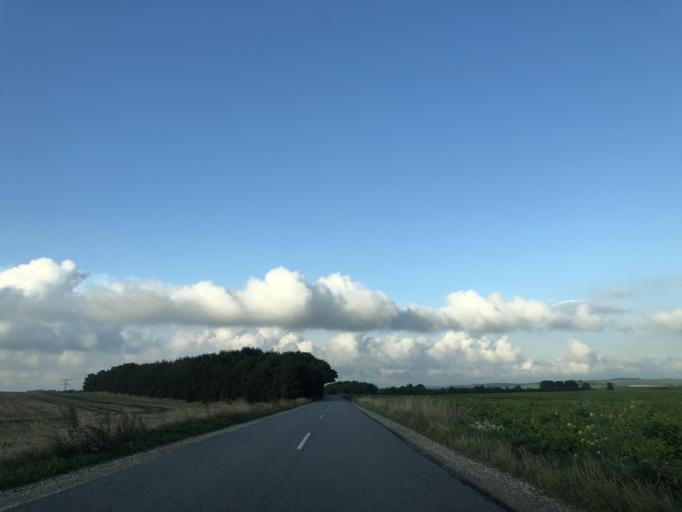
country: DK
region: North Denmark
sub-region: Rebild Kommune
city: Stovring
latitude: 56.9122
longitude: 9.7477
